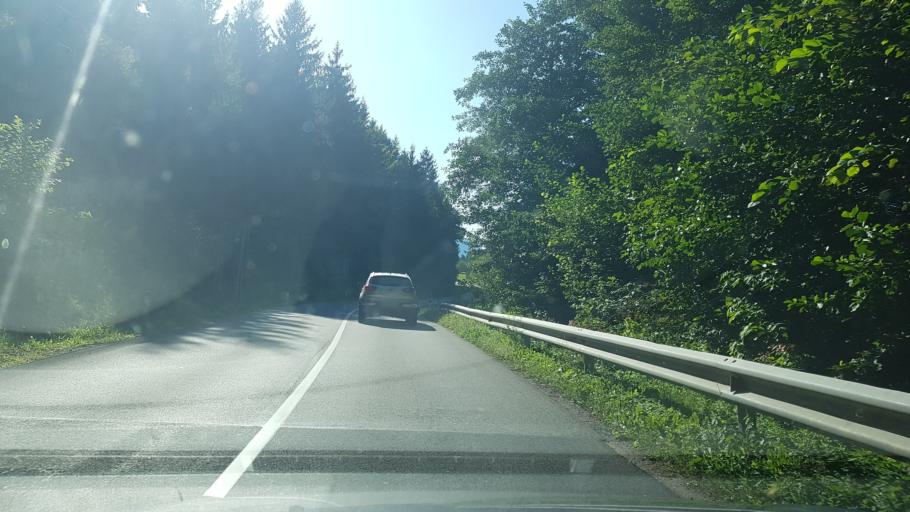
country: SI
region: Ravne na Koroskem
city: Kotlje
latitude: 46.5158
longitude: 15.0099
